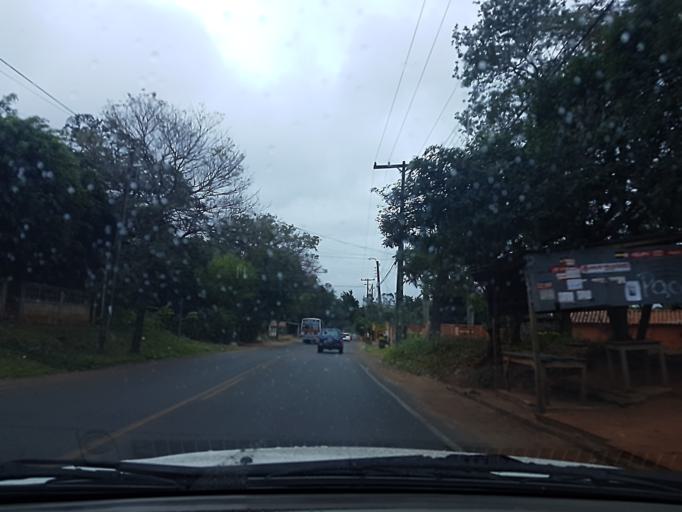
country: PY
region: Central
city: Limpio
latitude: -25.2523
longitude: -57.5018
